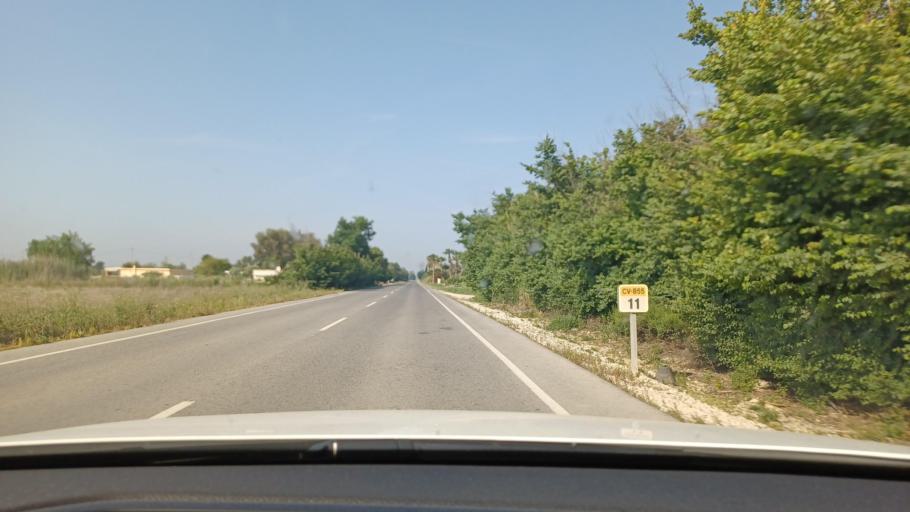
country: ES
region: Valencia
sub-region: Provincia de Alicante
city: Daya Vieja
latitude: 38.1555
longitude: -0.7086
